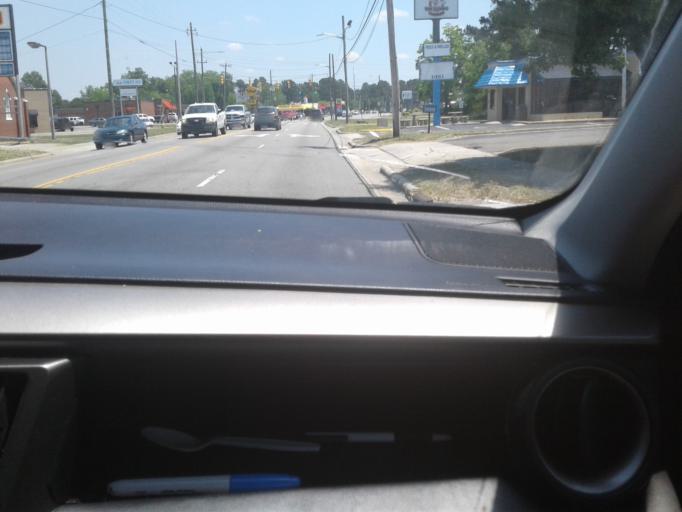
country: US
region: North Carolina
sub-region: Harnett County
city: Dunn
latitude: 35.3027
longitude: -78.6026
